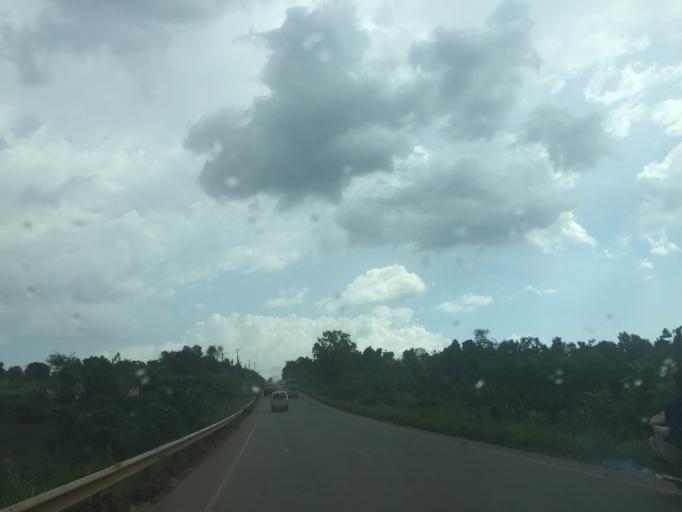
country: UG
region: Central Region
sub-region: Luwero District
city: Wobulenzi
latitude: 0.6025
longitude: 32.5322
